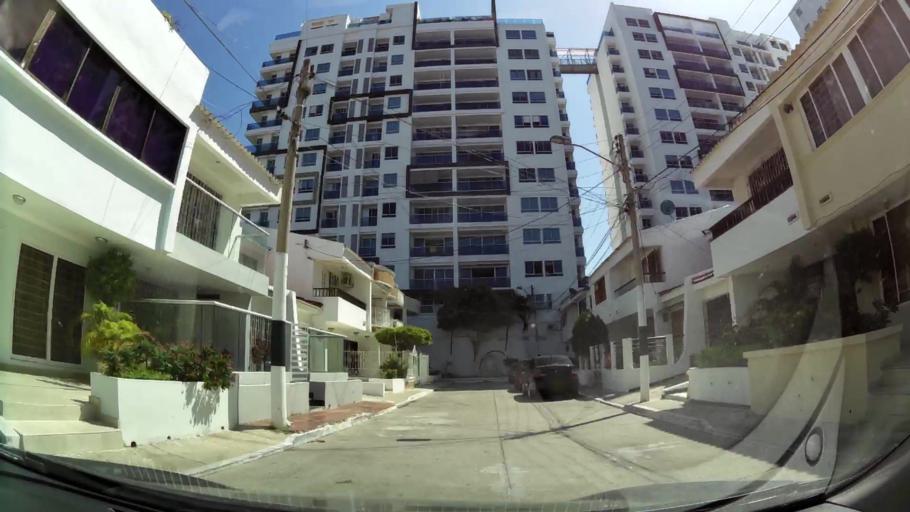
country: CO
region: Bolivar
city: Cartagena
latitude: 10.4436
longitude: -75.5216
